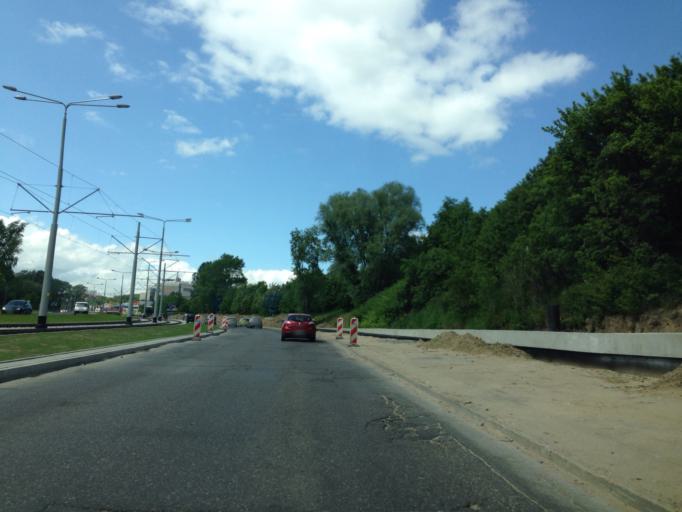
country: PL
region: Pomeranian Voivodeship
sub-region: Gdansk
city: Gdansk
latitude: 54.3491
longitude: 18.6015
